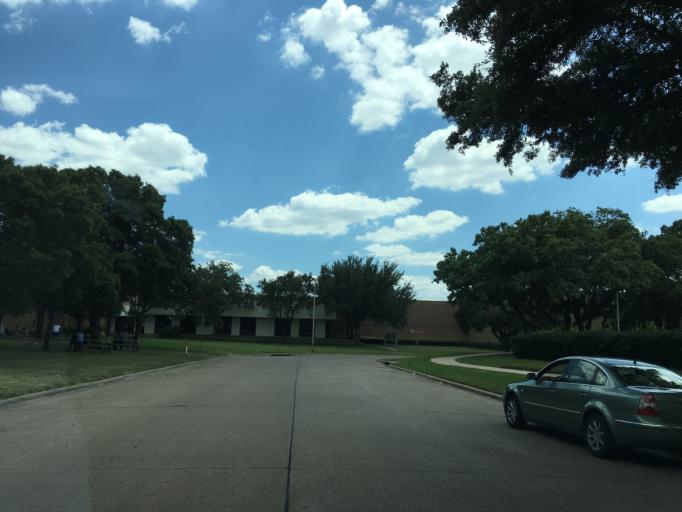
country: US
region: Texas
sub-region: Dallas County
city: Addison
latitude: 32.9485
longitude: -96.8324
